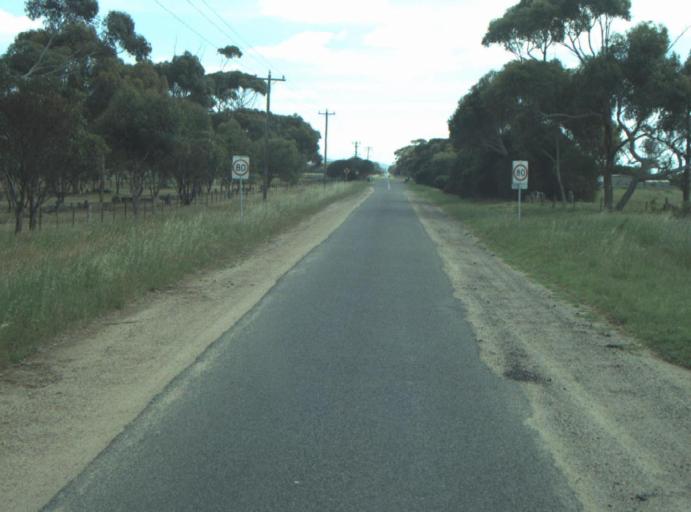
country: AU
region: Victoria
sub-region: Greater Geelong
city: Lara
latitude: -38.0584
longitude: 144.4271
